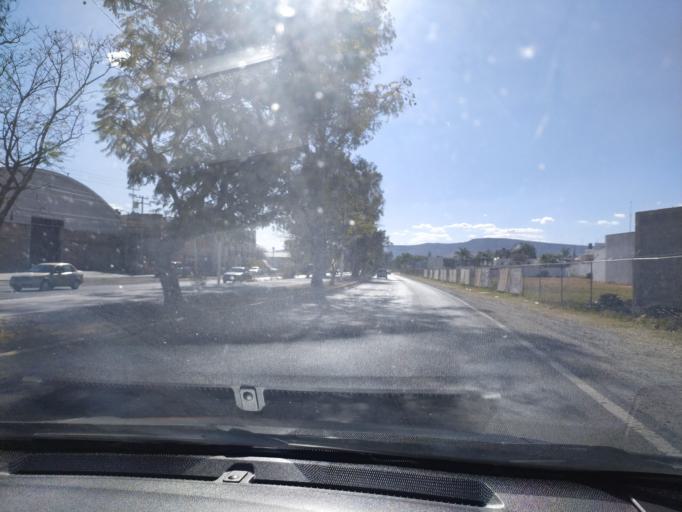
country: LA
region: Oudomxai
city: Muang La
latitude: 21.0315
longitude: 101.8421
